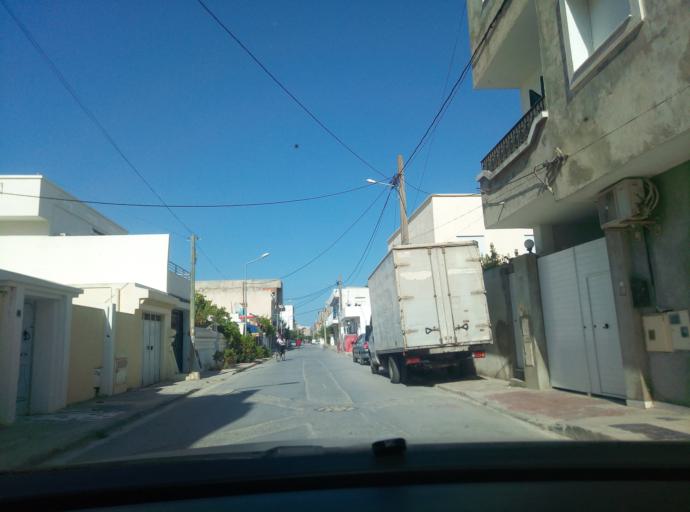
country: TN
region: Tunis
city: La Goulette
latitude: 36.8531
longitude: 10.2636
